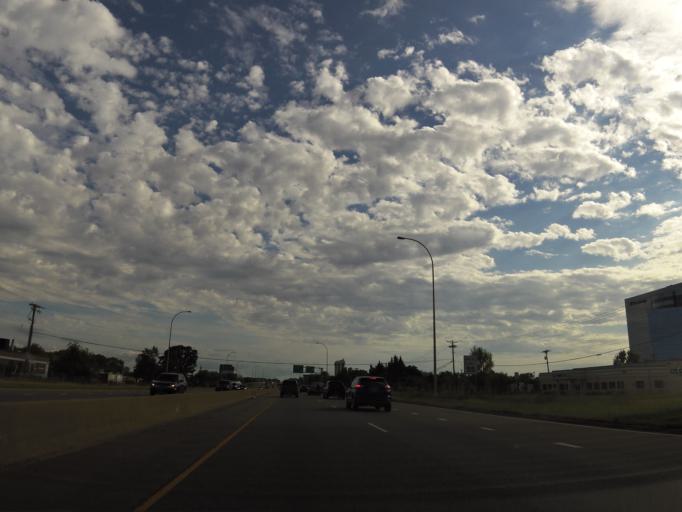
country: US
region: Minnesota
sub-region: Hennepin County
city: New Hope
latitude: 44.9881
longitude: -93.4008
